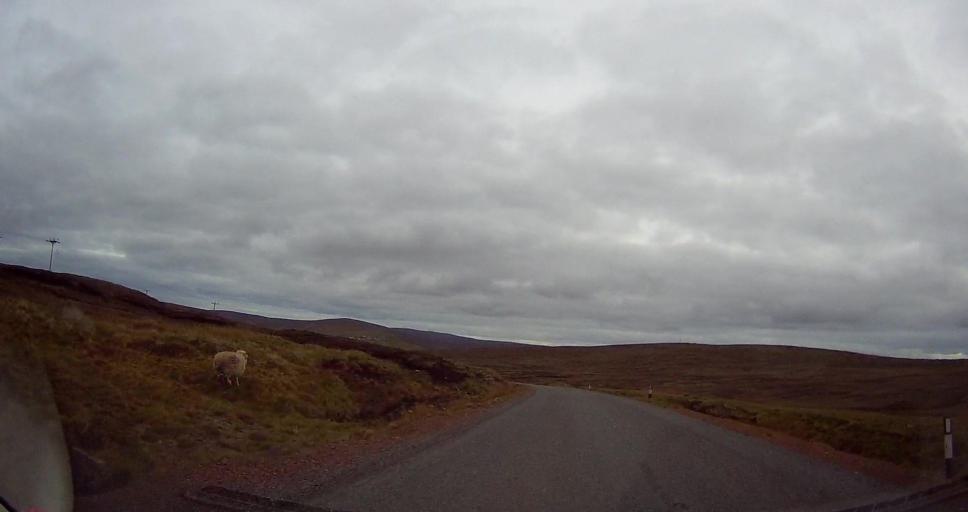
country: GB
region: Scotland
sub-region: Shetland Islands
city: Shetland
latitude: 60.6254
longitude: -1.0725
